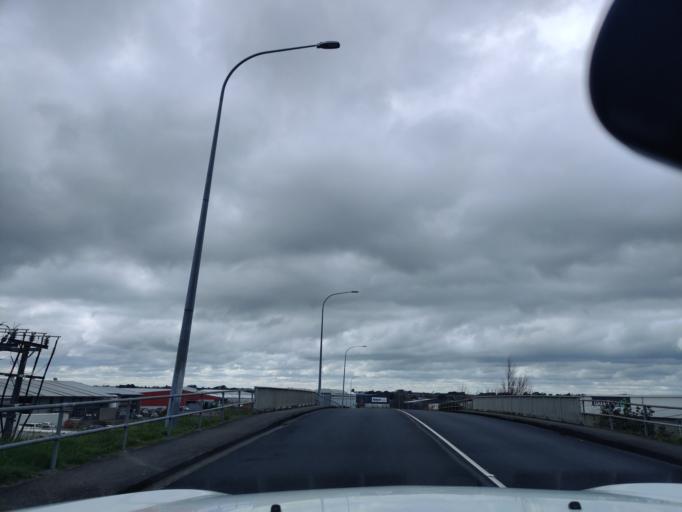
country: NZ
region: Manawatu-Wanganui
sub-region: Palmerston North City
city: Palmerston North
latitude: -40.3377
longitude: 175.6438
